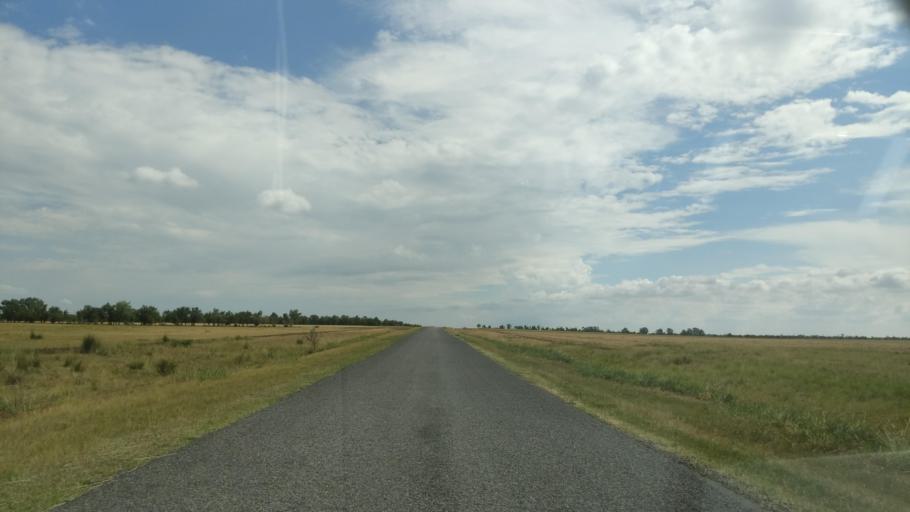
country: KZ
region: Pavlodar
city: Pavlodar
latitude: 52.6365
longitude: 76.9583
